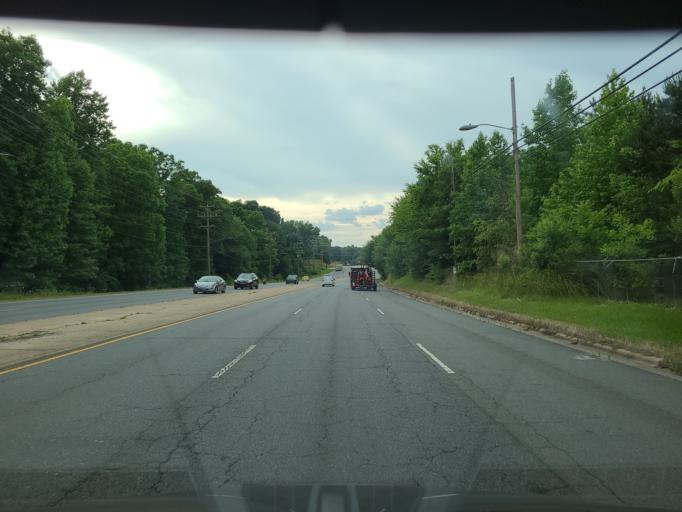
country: US
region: North Carolina
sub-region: Gaston County
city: Belmont
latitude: 35.2365
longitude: -80.9563
